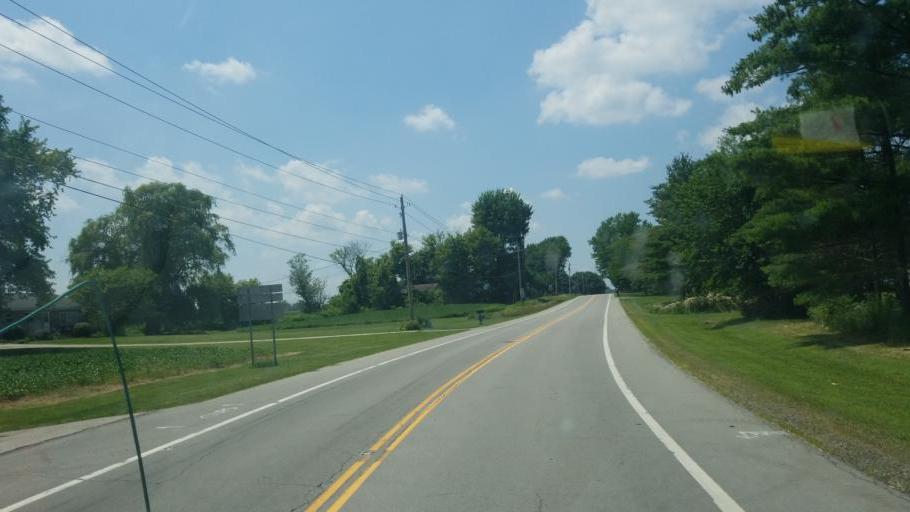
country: US
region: Ohio
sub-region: Richland County
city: Shelby
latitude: 40.8501
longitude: -82.6636
